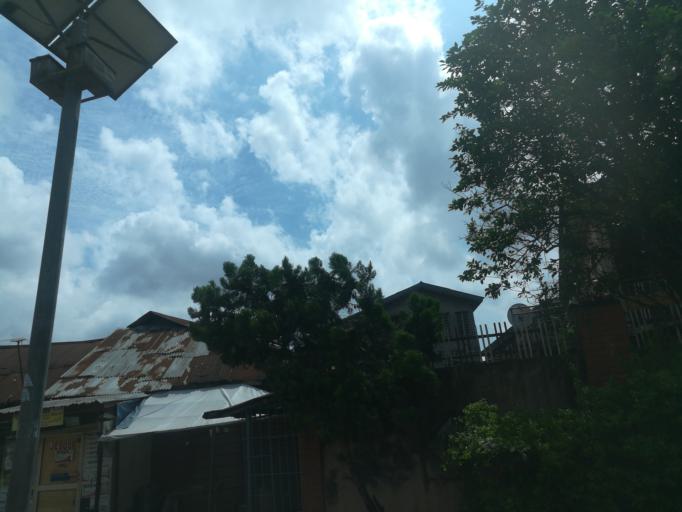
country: NG
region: Lagos
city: Somolu
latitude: 6.5352
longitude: 3.3645
